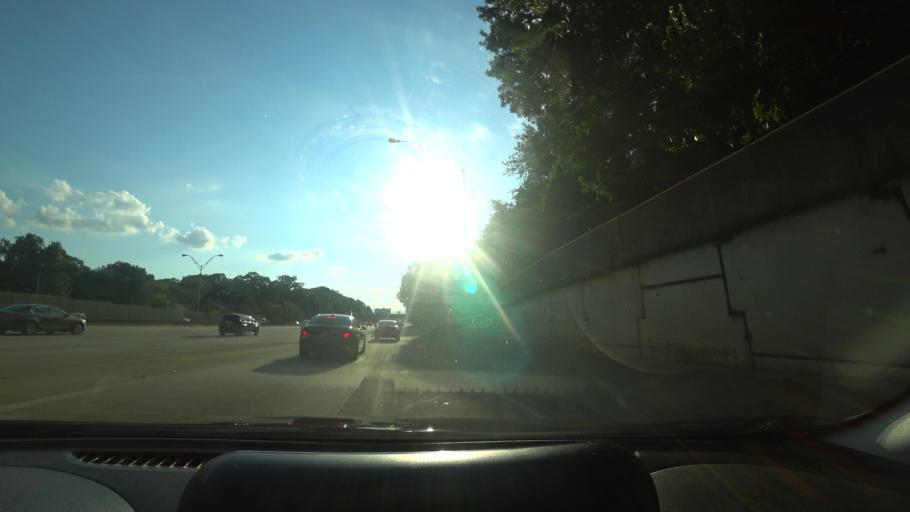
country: US
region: Georgia
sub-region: Fulton County
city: Atlanta
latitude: 33.7438
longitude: -84.3701
